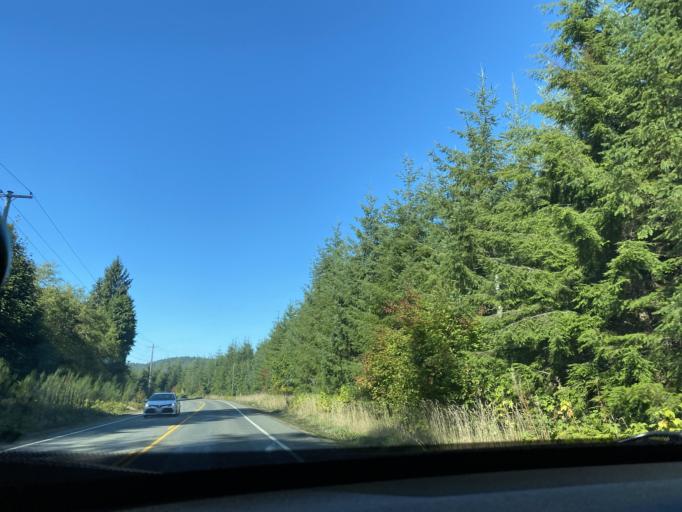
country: US
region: Washington
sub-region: Clallam County
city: Forks
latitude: 47.9637
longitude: -124.4319
